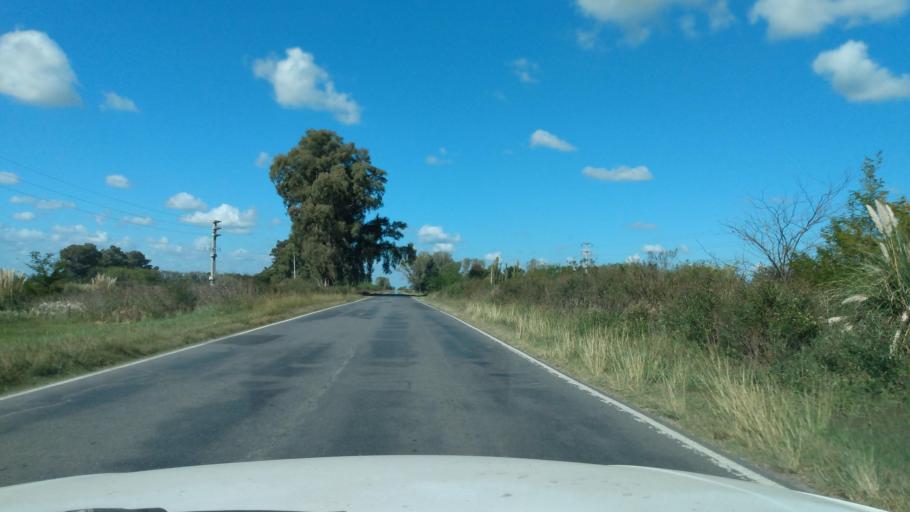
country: AR
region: Buenos Aires
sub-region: Partido de Mercedes
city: Mercedes
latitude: -34.7054
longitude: -59.4017
